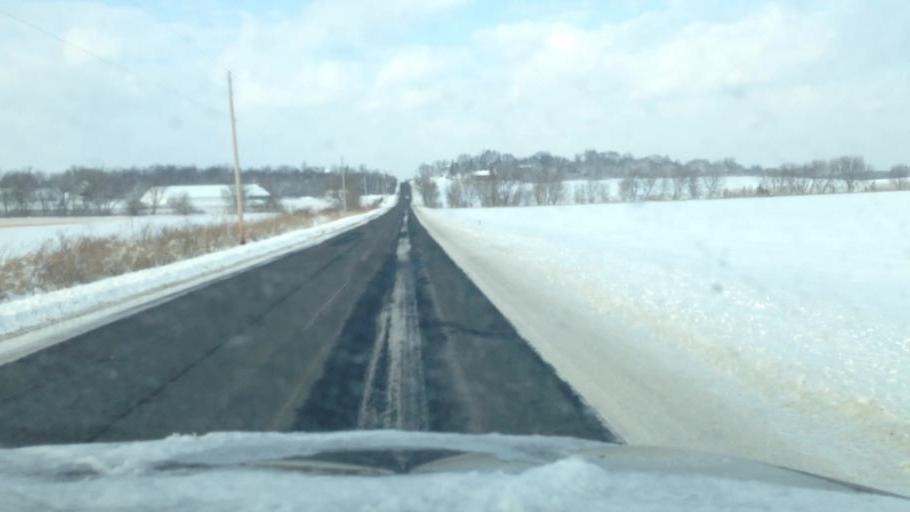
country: US
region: Wisconsin
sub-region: Walworth County
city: East Troy
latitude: 42.7680
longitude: -88.4454
